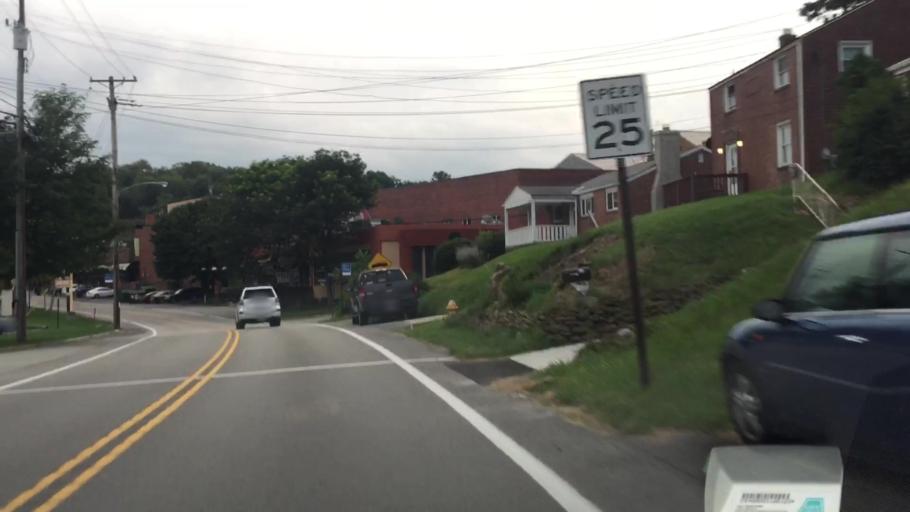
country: US
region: Pennsylvania
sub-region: Allegheny County
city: Whitehall
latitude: 40.3604
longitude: -80.0009
